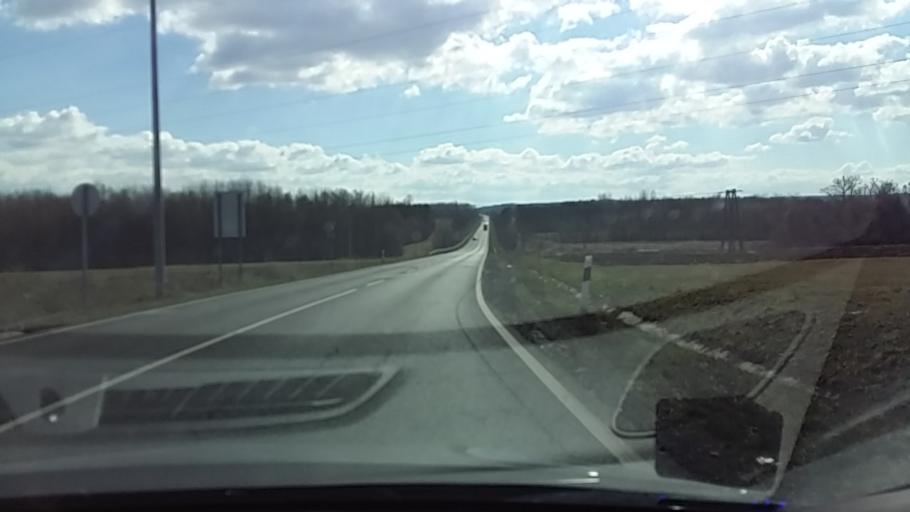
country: HU
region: Baranya
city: Kozarmisleny
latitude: 46.0538
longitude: 18.2758
